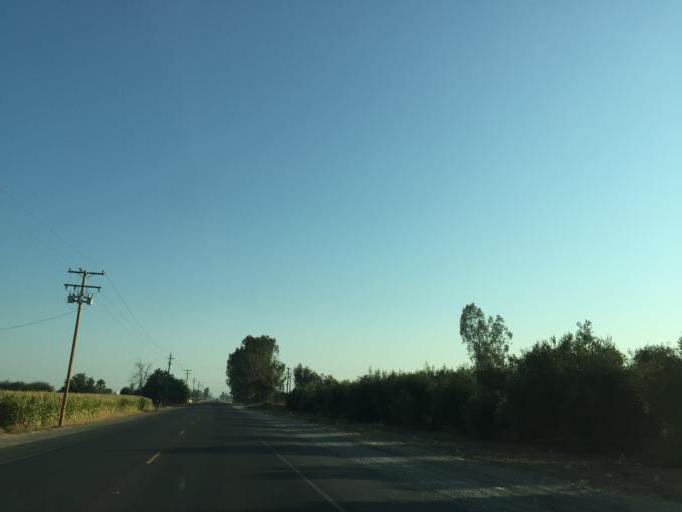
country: US
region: California
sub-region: Tulare County
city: Cutler
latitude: 36.4417
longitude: -119.2956
